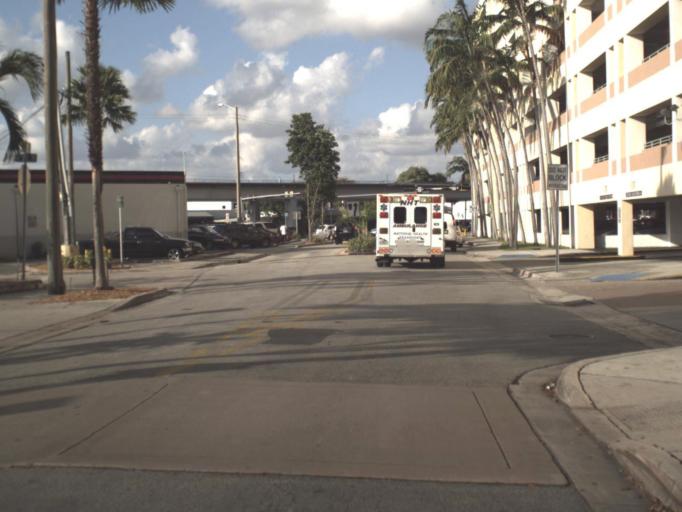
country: US
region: Florida
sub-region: Miami-Dade County
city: South Miami
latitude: 25.7049
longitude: -80.2874
